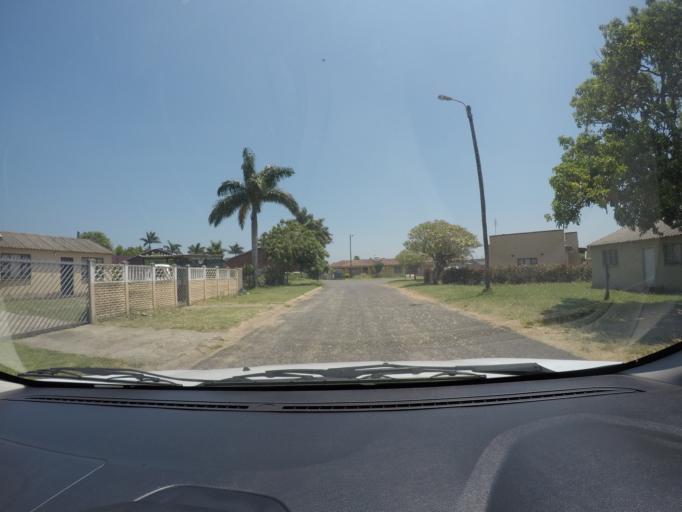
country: ZA
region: KwaZulu-Natal
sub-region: uThungulu District Municipality
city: eSikhawini
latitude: -28.8852
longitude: 31.8872
